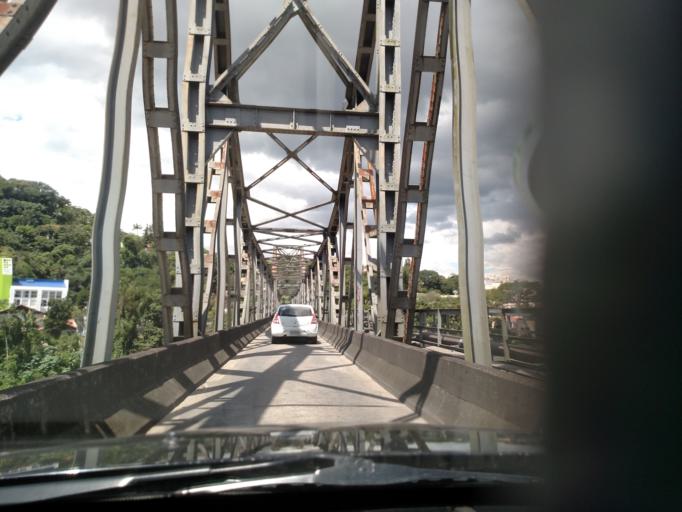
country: BR
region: Santa Catarina
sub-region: Blumenau
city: Blumenau
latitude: -26.9127
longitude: -49.0687
